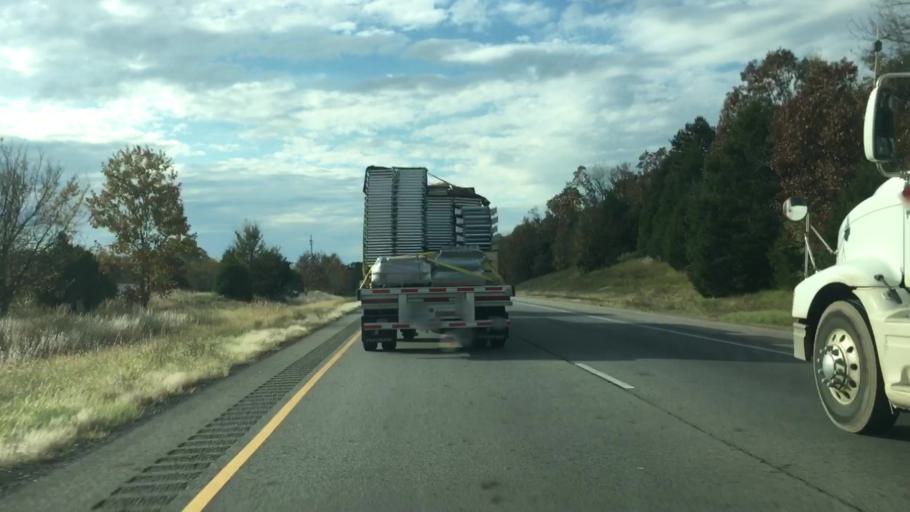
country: US
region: Arkansas
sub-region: Pope County
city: Pottsville
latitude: 35.2472
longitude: -93.0053
